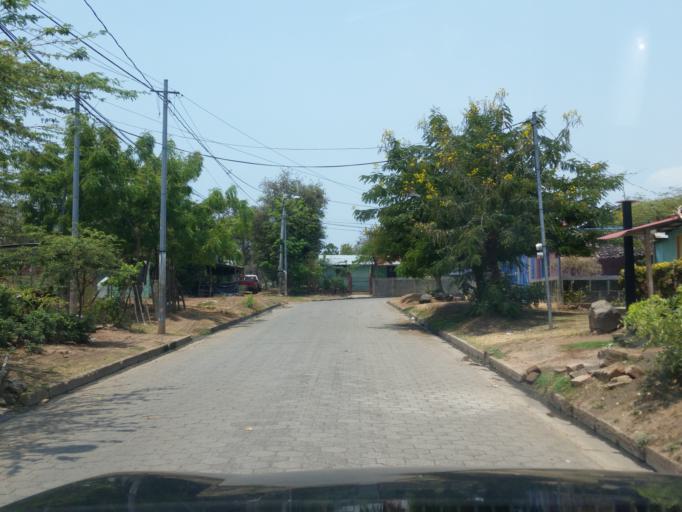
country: NI
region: Granada
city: Granada
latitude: 11.9346
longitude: -85.9718
